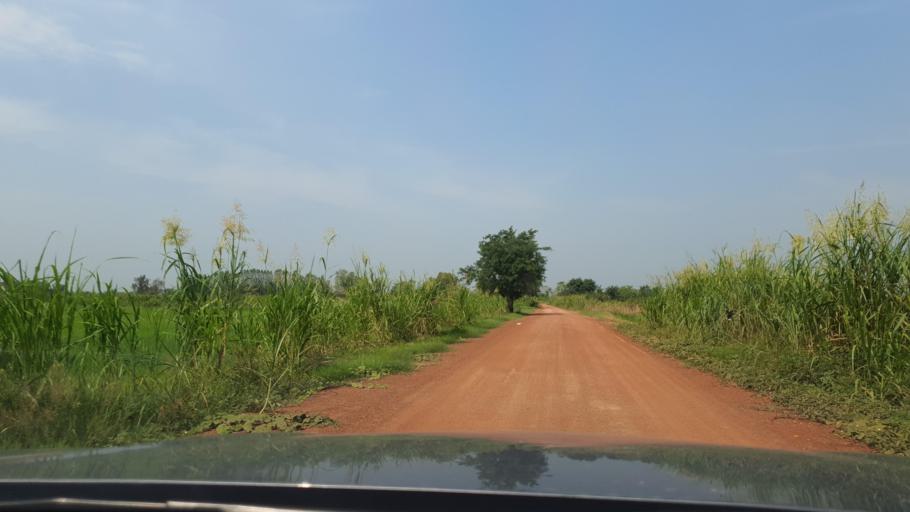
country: TH
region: Phitsanulok
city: Bang Rakam
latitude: 16.7998
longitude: 100.1095
